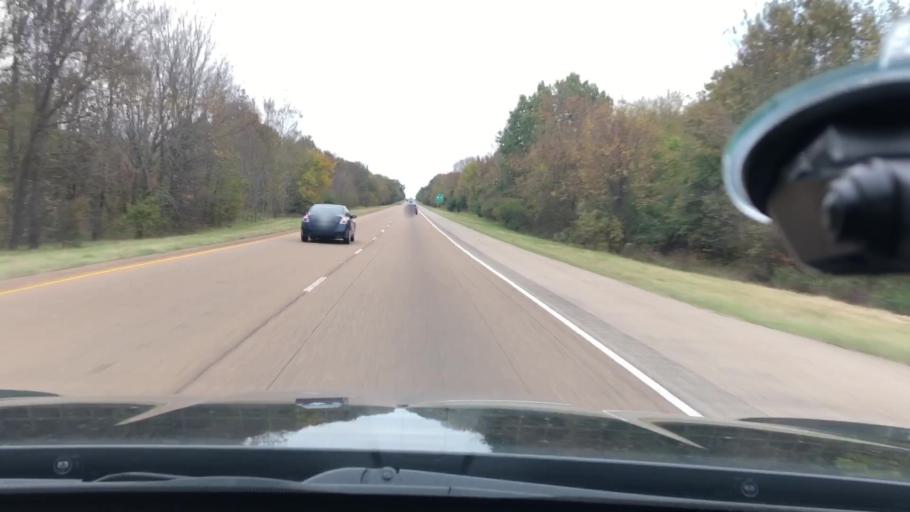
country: US
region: Arkansas
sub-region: Nevada County
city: Prescott
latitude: 33.7974
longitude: -93.4410
